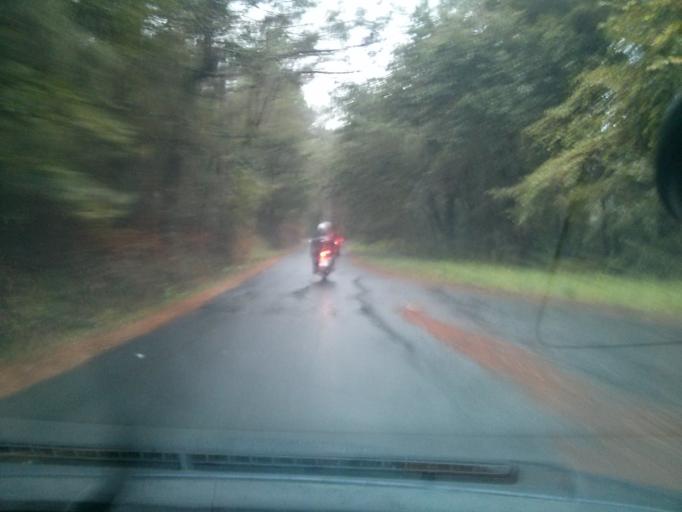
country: ES
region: Galicia
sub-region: Provincia da Coruna
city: Outes
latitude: 42.8362
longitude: -8.8656
